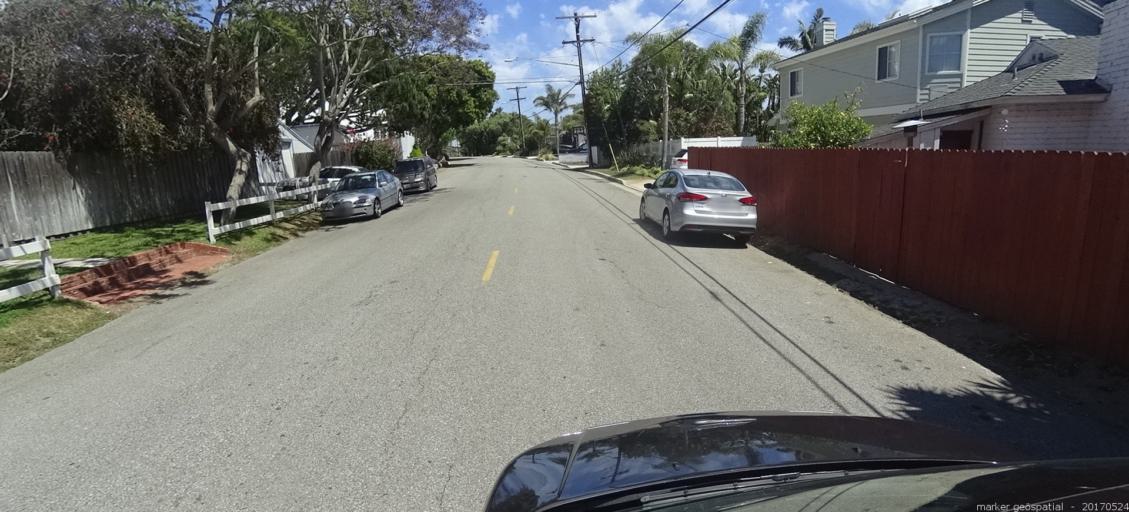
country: US
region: California
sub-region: Los Angeles County
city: Redondo Beach
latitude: 33.8303
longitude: -118.3827
